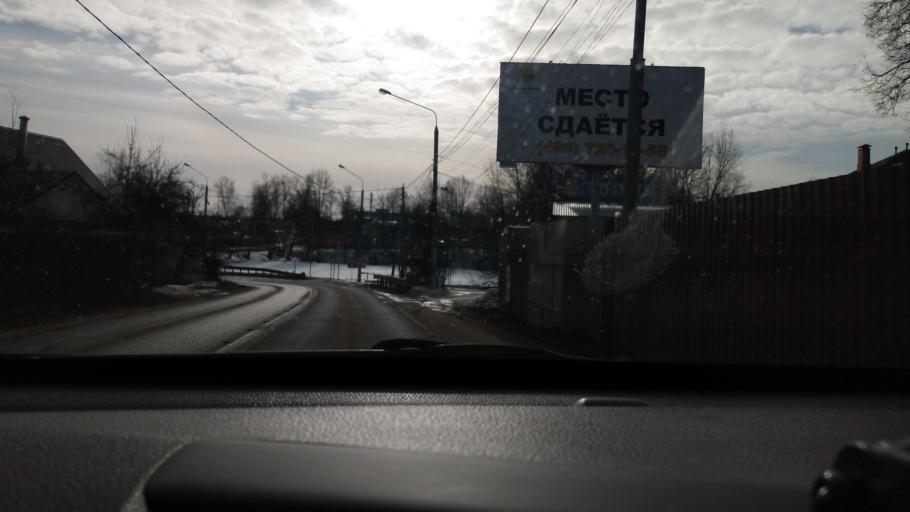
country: RU
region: Moskovskaya
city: Nakhabino
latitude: 55.8681
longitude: 37.1839
